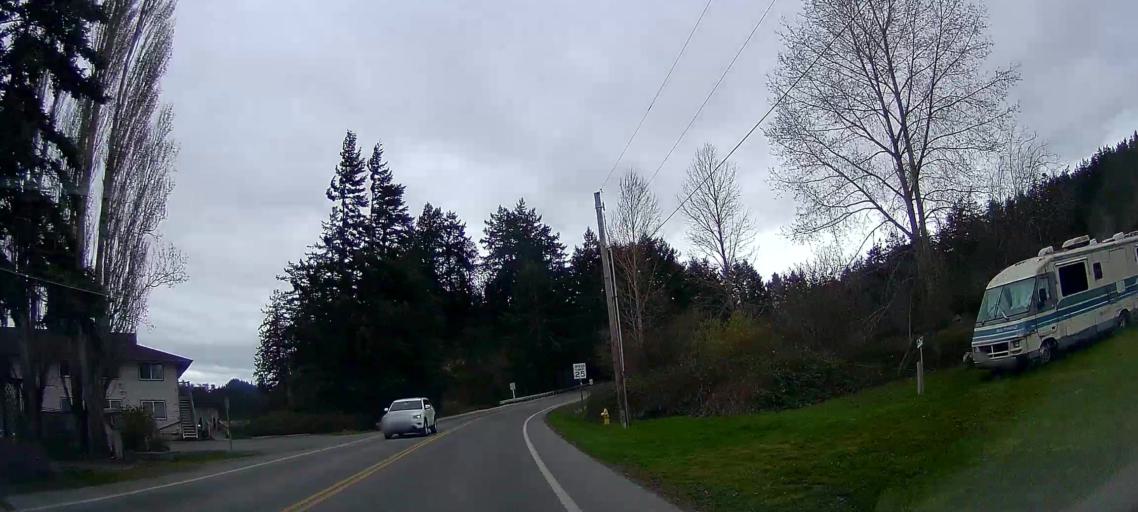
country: US
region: Washington
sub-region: Skagit County
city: Mount Vernon
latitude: 48.3850
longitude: -122.4953
